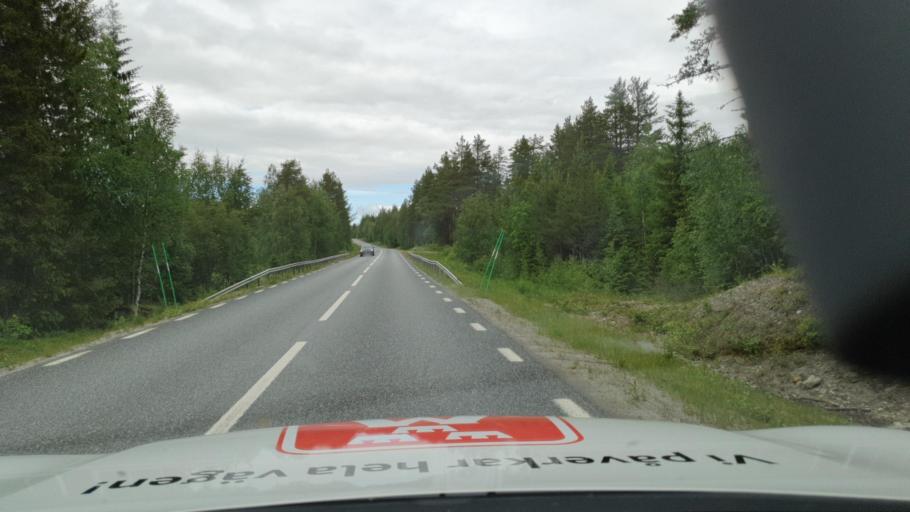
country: SE
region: Vaesterbotten
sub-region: Asele Kommun
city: Insjon
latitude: 64.2348
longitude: 17.5510
